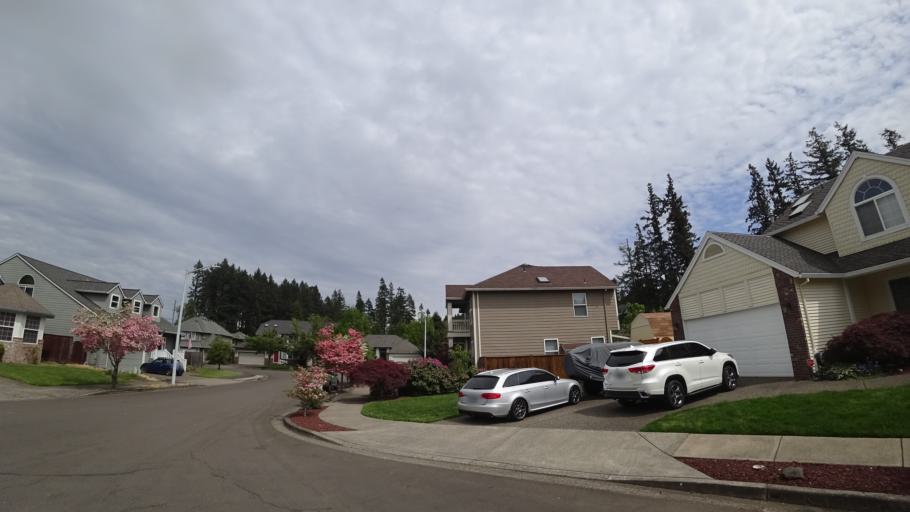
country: US
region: Oregon
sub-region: Washington County
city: Rockcreek
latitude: 45.5187
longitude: -122.9225
